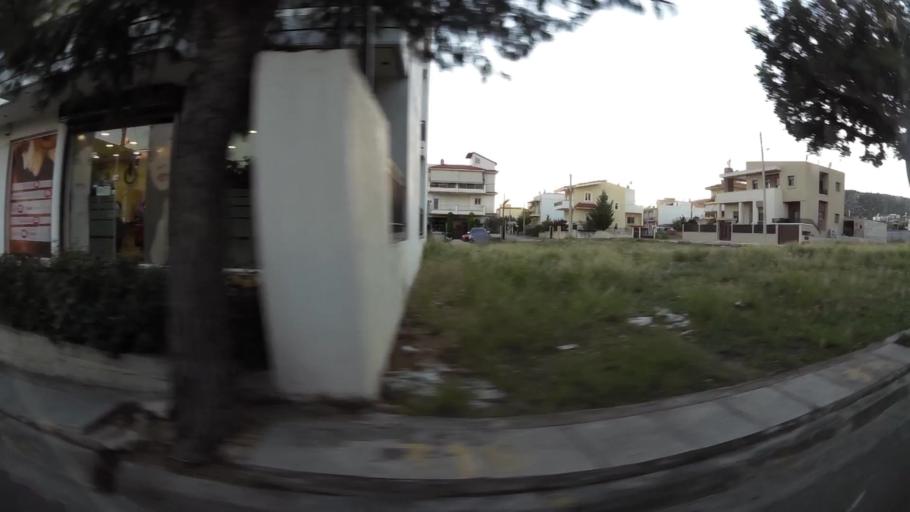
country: GR
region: Attica
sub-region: Nomarchia Dytikis Attikis
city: Ano Liosia
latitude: 38.0881
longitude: 23.6961
